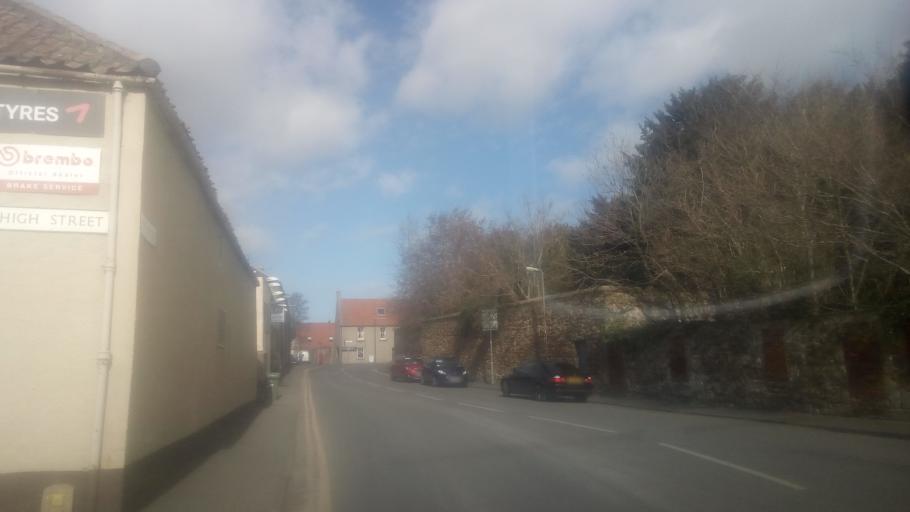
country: GB
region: Scotland
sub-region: East Lothian
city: Ormiston
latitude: 55.9121
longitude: -2.9399
